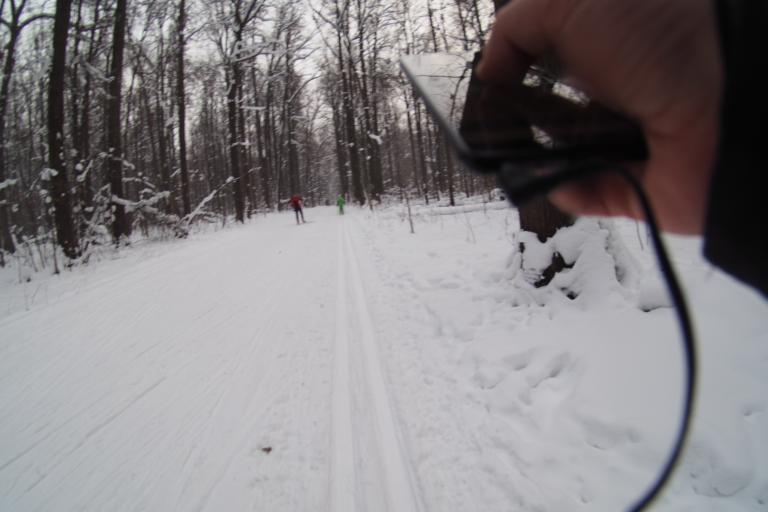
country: RU
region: Moskovskaya
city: Izmaylovo
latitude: 55.7704
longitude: 37.7773
